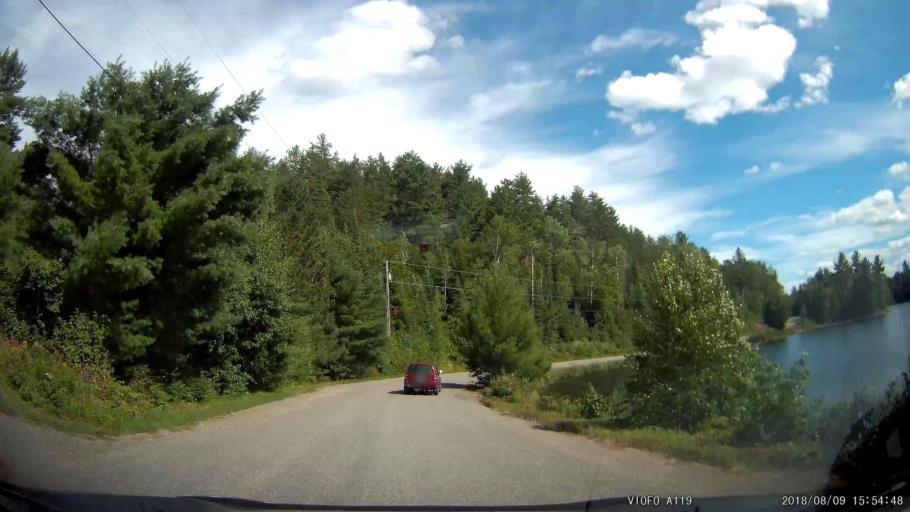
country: CA
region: Ontario
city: Rayside-Balfour
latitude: 46.6066
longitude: -81.5274
